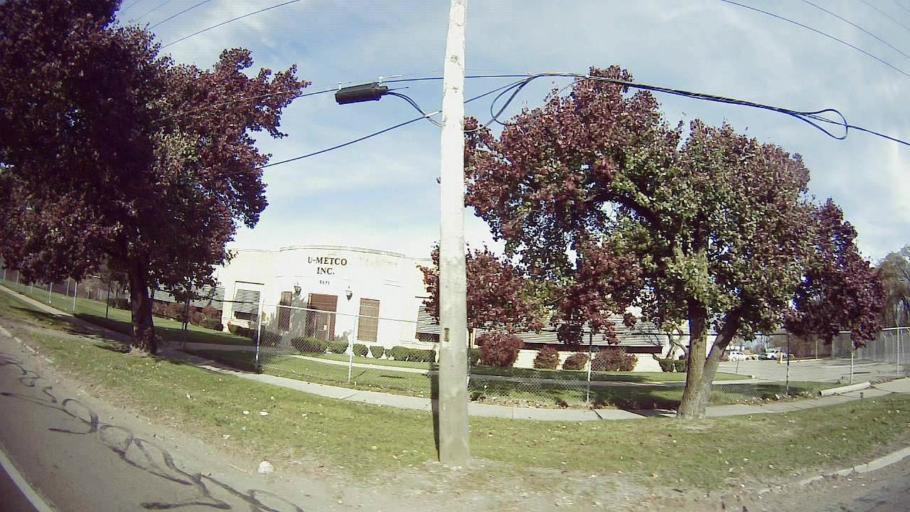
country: US
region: Michigan
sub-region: Macomb County
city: Warren
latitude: 42.4341
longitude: -83.0170
